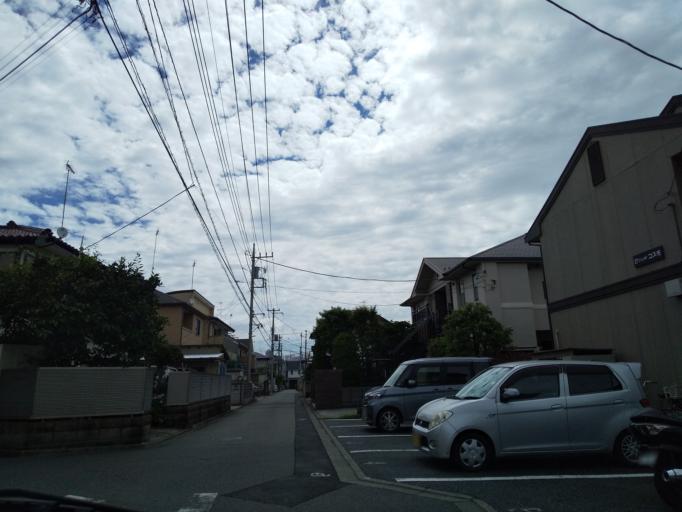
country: JP
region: Kanagawa
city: Zama
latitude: 35.5561
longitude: 139.3730
